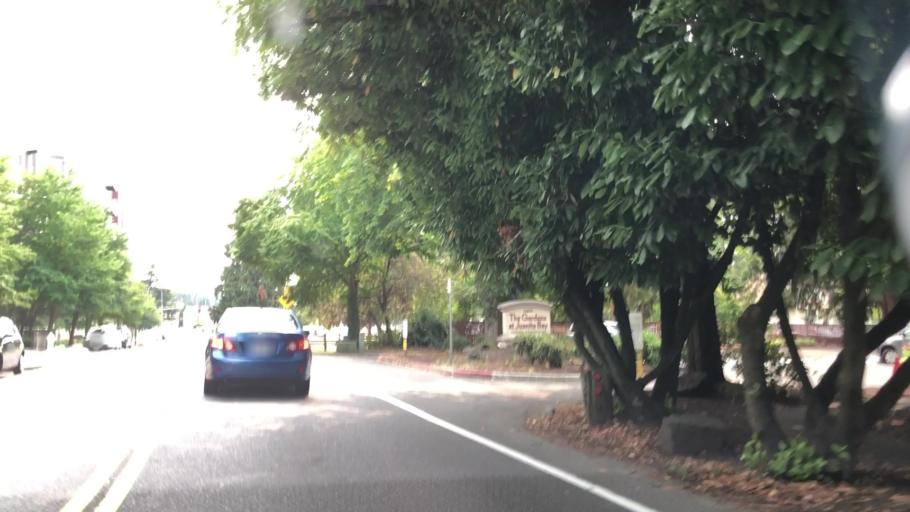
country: US
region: Washington
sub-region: King County
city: Inglewood-Finn Hill
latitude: 47.7071
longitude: -122.2126
